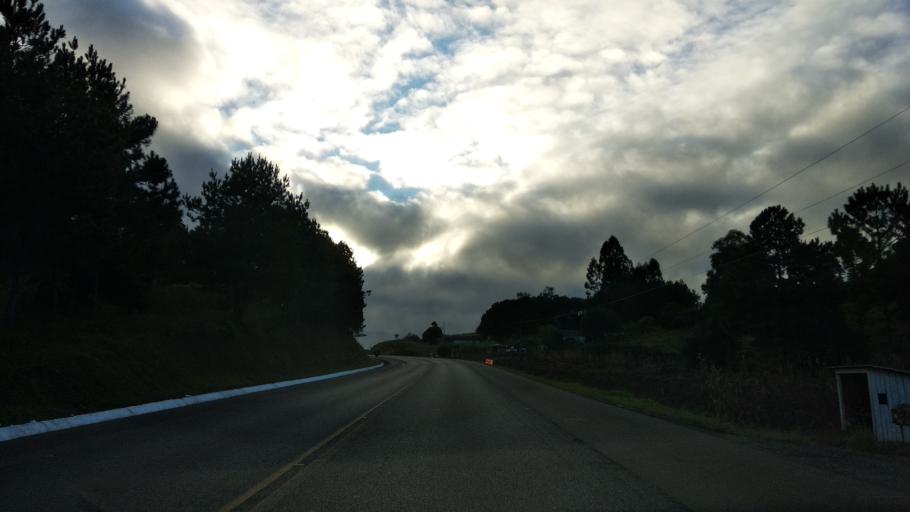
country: BR
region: Santa Catarina
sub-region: Curitibanos
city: Curitibanos
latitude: -27.5611
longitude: -50.8361
